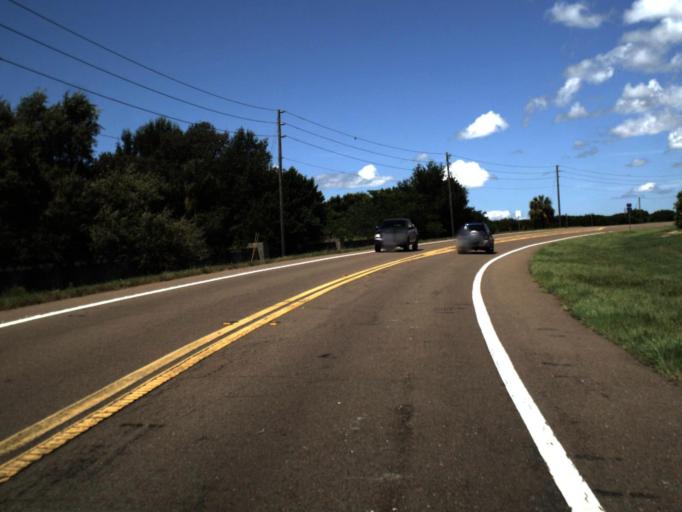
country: US
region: Florida
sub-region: Polk County
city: Lake Wales
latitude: 27.8695
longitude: -81.5799
